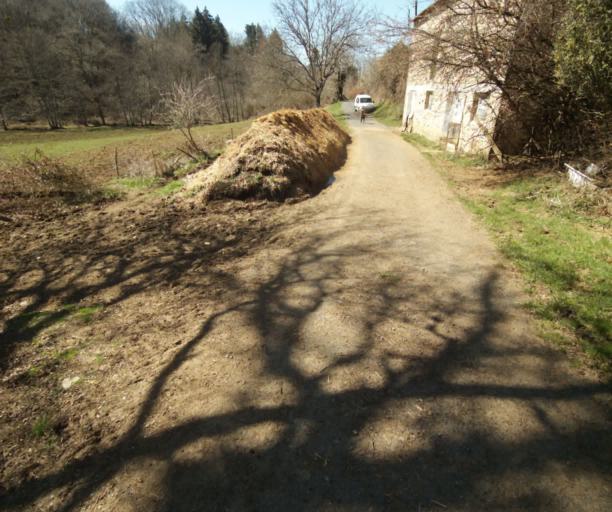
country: FR
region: Limousin
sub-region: Departement de la Correze
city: Chamboulive
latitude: 45.4383
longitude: 1.7317
